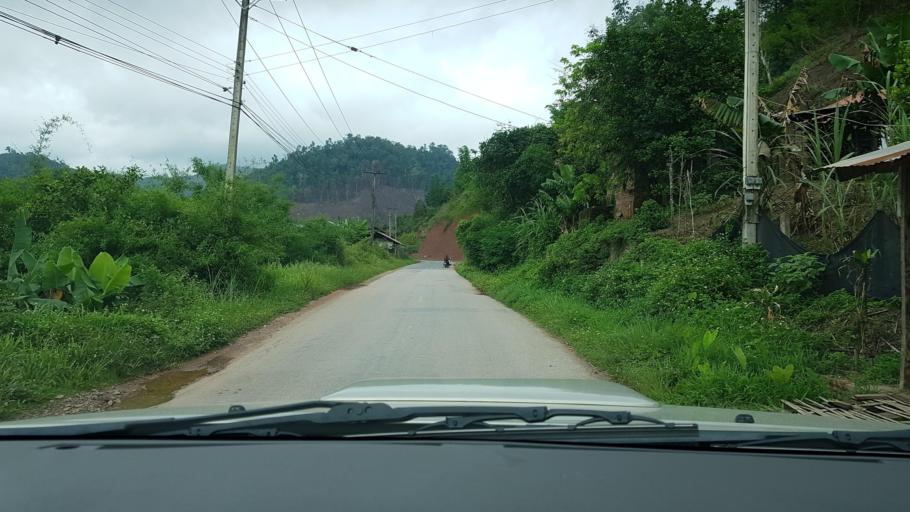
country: LA
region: Oudomxai
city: Muang Xay
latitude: 20.5840
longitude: 101.9231
